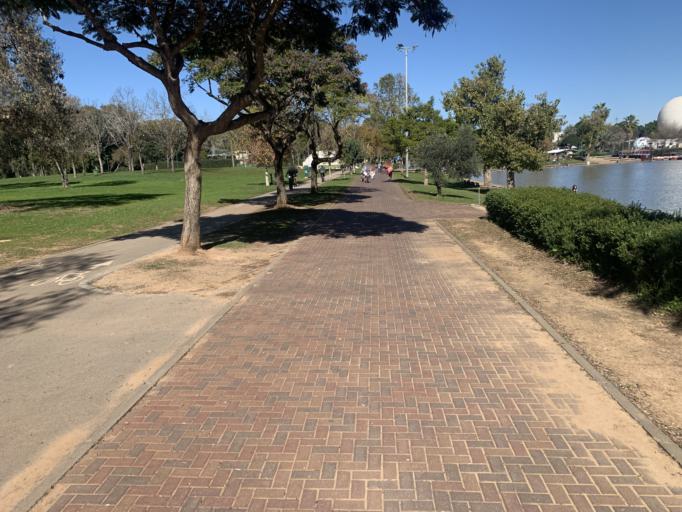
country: IL
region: Tel Aviv
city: Ramat Gan
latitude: 32.0972
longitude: 34.8094
